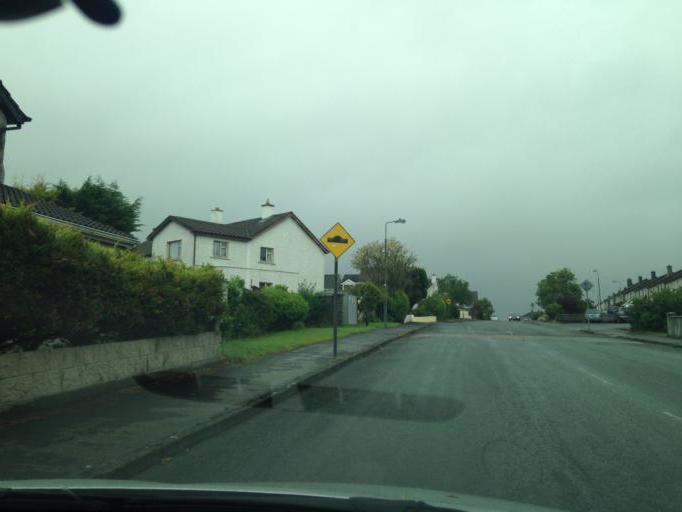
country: IE
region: Connaught
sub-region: County Galway
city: Gaillimh
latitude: 53.2874
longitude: -9.0314
